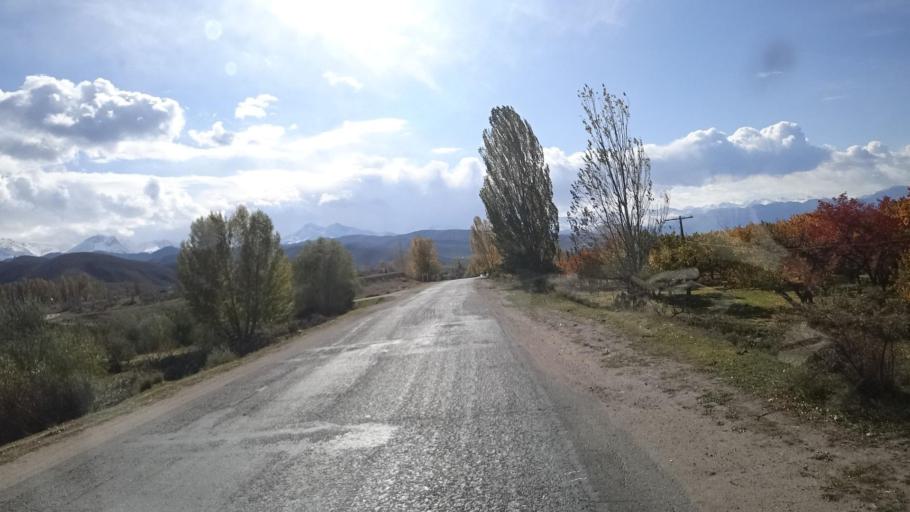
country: KG
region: Ysyk-Koel
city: Pokrovka
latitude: 42.2277
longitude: 77.7141
